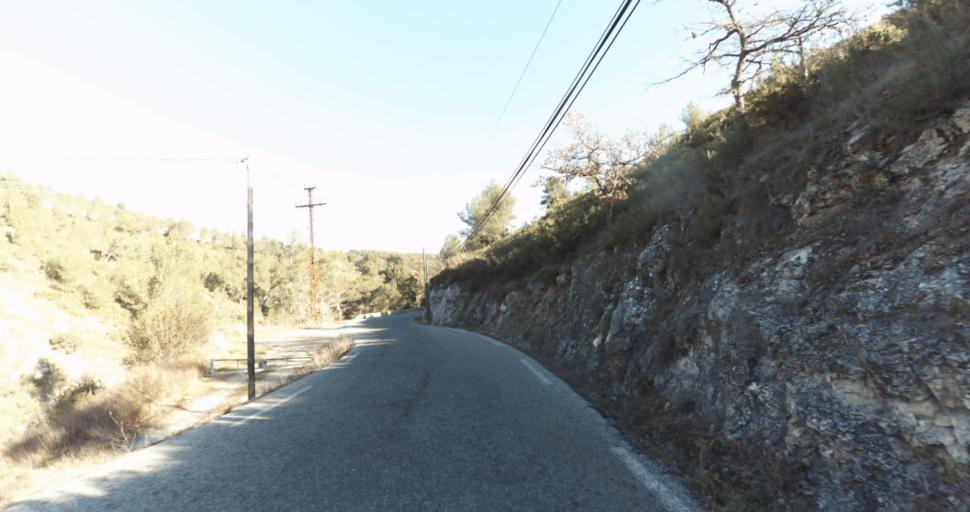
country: FR
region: Provence-Alpes-Cote d'Azur
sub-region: Departement des Bouches-du-Rhone
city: Peypin
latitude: 43.3814
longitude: 5.5678
